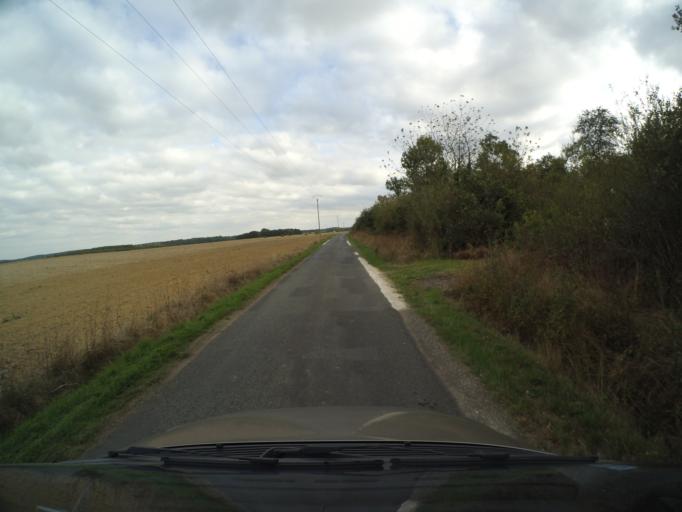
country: FR
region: Centre
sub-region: Departement d'Indre-et-Loire
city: Nazelles-Negron
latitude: 47.4809
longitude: 0.9526
